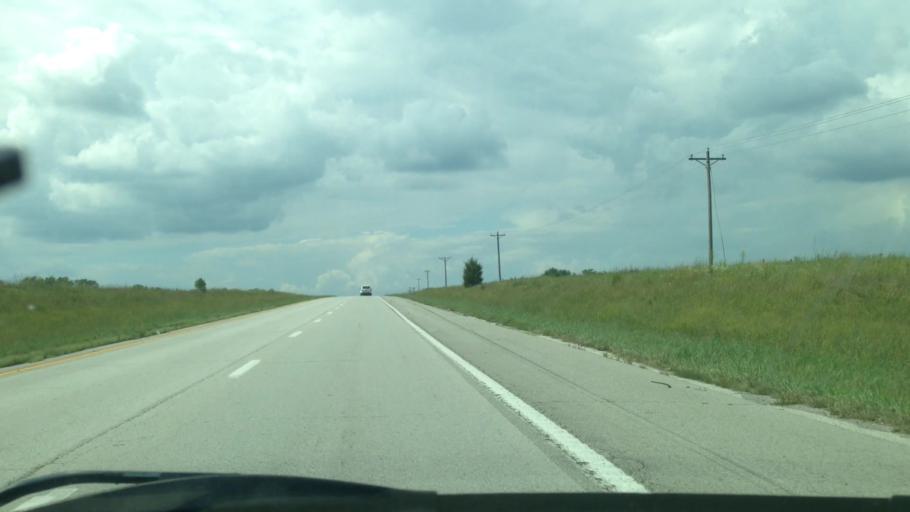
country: US
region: Missouri
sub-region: Pike County
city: Bowling Green
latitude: 39.2627
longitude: -91.0719
